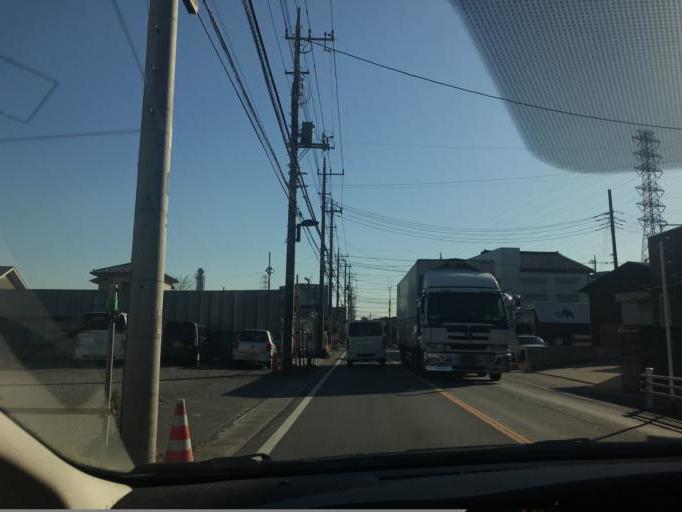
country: JP
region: Saitama
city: Yashio-shi
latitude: 35.8373
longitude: 139.8361
